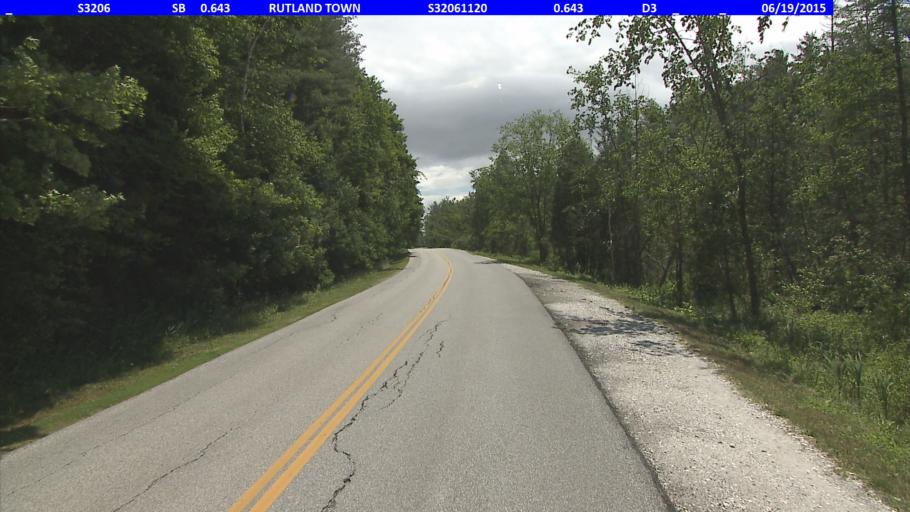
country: US
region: Vermont
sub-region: Rutland County
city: Rutland
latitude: 43.6386
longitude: -72.9917
